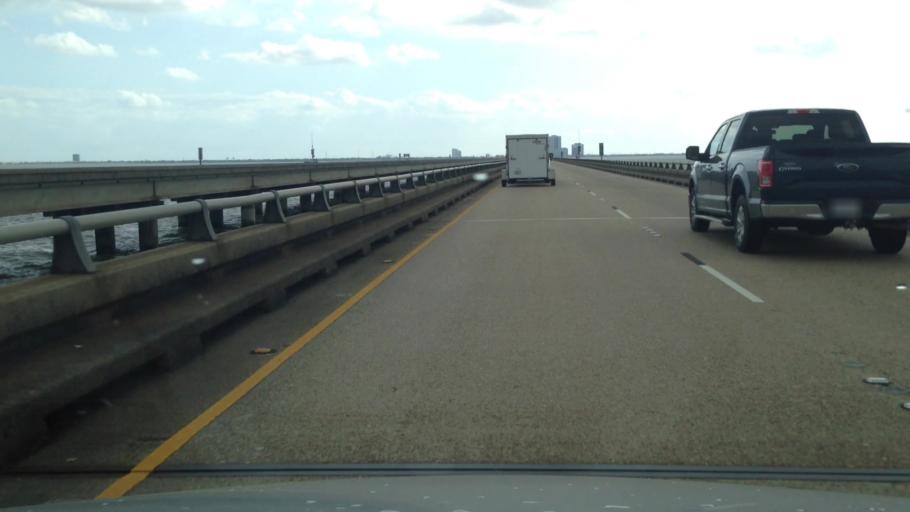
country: US
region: Louisiana
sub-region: Jefferson Parish
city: Metairie
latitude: 30.0657
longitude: -90.1463
